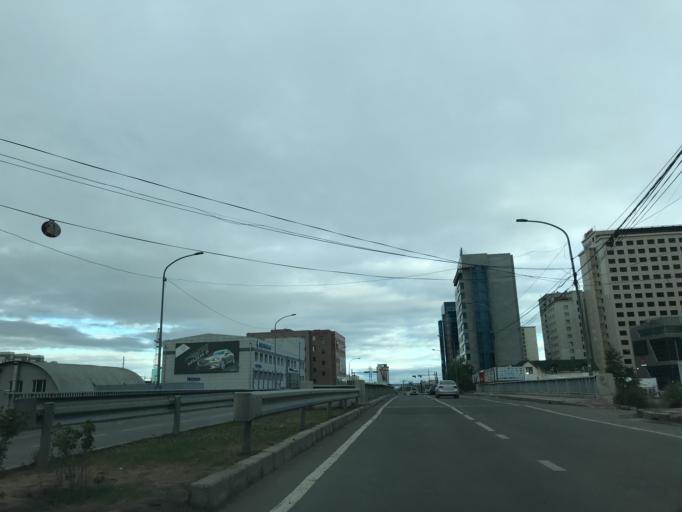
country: MN
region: Ulaanbaatar
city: Ulaanbaatar
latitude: 47.9082
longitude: 106.9332
